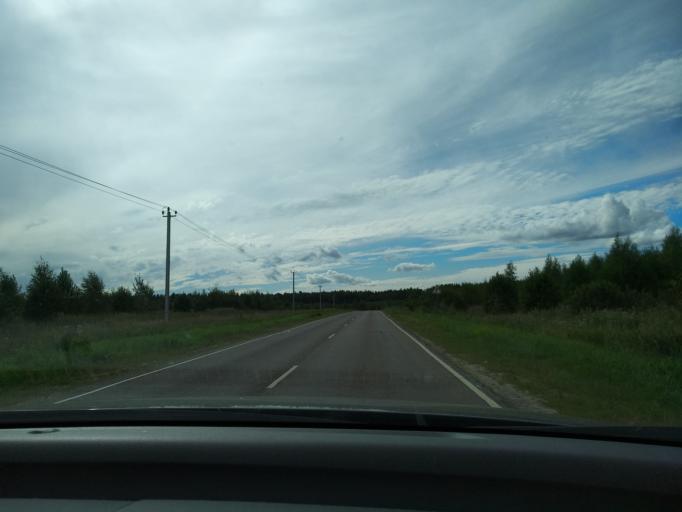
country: RU
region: Moskovskaya
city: Krasnyy Tkach
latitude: 55.3926
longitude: 39.1456
